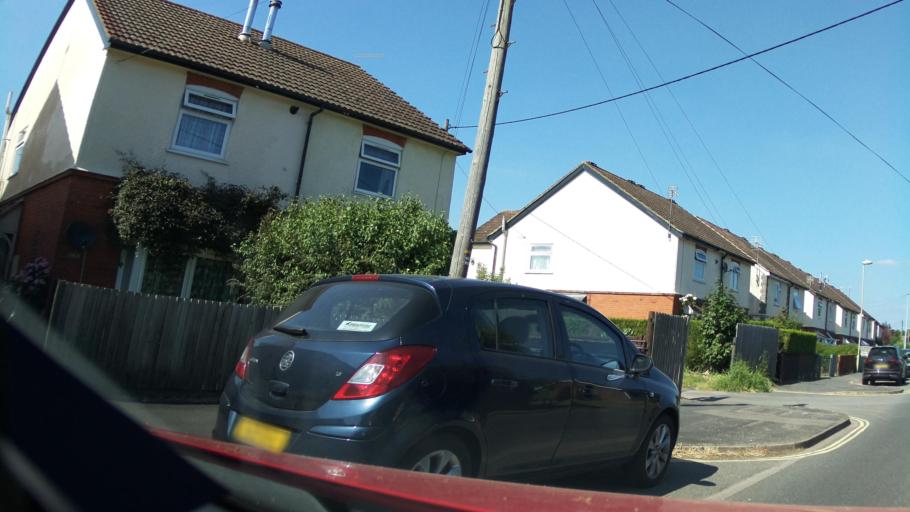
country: GB
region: England
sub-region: Hampshire
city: Andover
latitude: 51.2123
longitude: -1.4691
